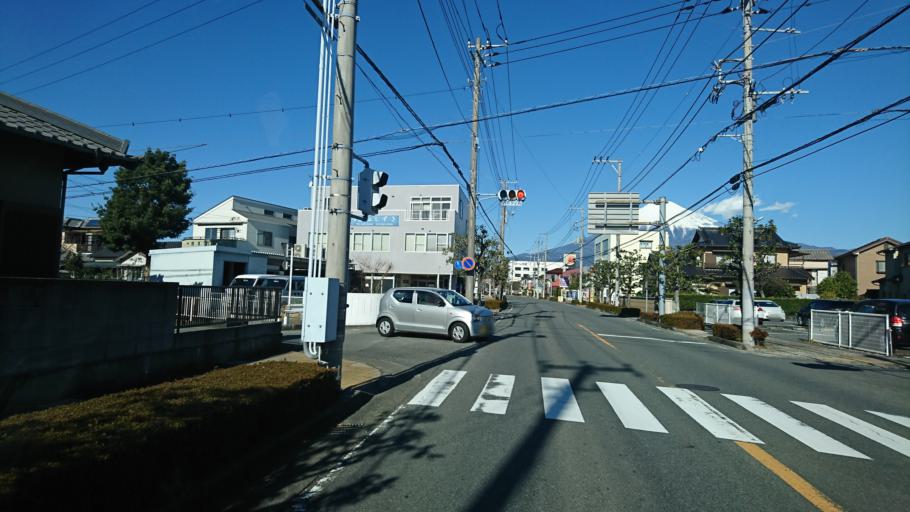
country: JP
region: Shizuoka
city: Fuji
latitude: 35.1633
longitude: 138.6535
